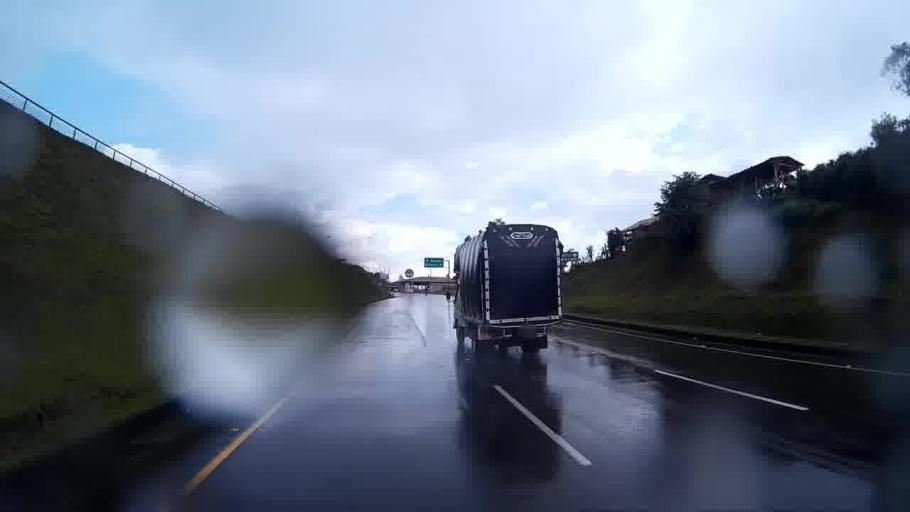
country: CO
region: Quindio
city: Filandia
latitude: 4.6902
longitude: -75.6071
